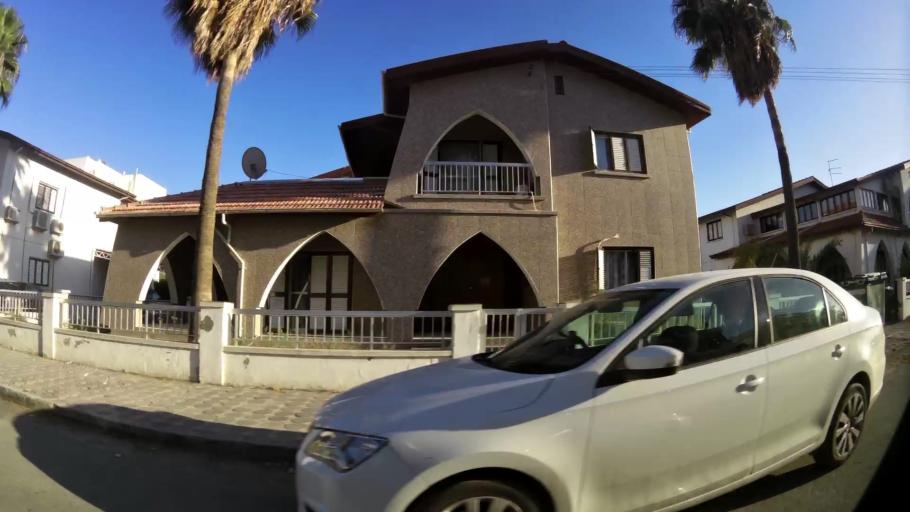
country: CY
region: Lefkosia
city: Nicosia
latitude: 35.2005
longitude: 33.3350
